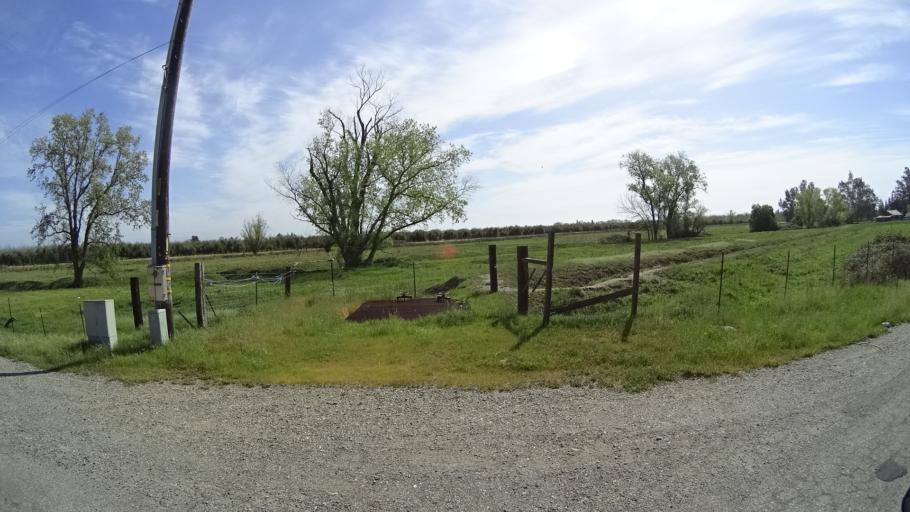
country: US
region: California
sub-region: Glenn County
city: Hamilton City
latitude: 39.6619
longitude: -122.0180
